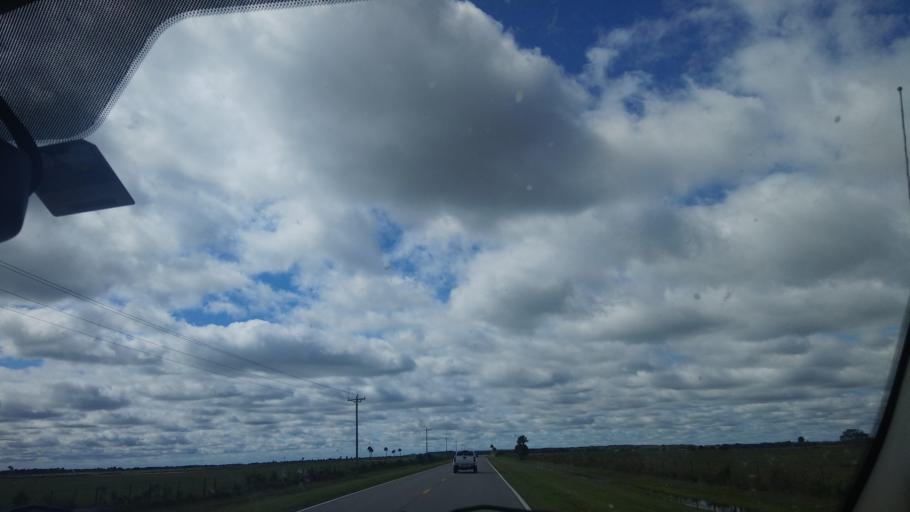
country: US
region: Florida
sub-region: Okeechobee County
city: Okeechobee
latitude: 27.3907
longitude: -80.9310
